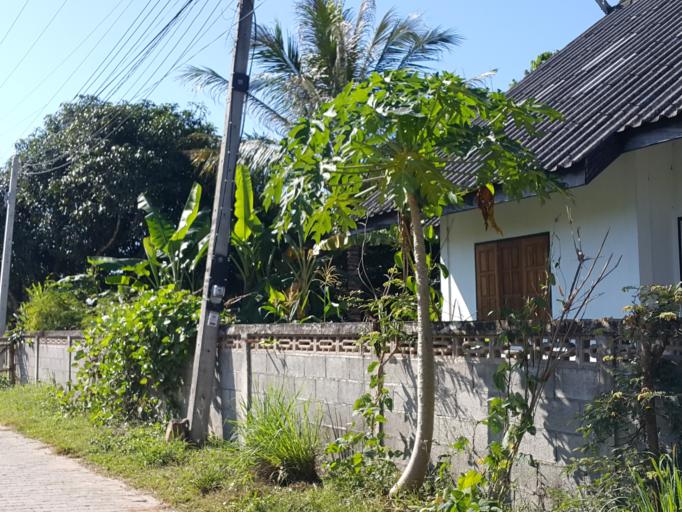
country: TH
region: Chiang Mai
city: Mae On
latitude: 18.7150
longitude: 99.2016
